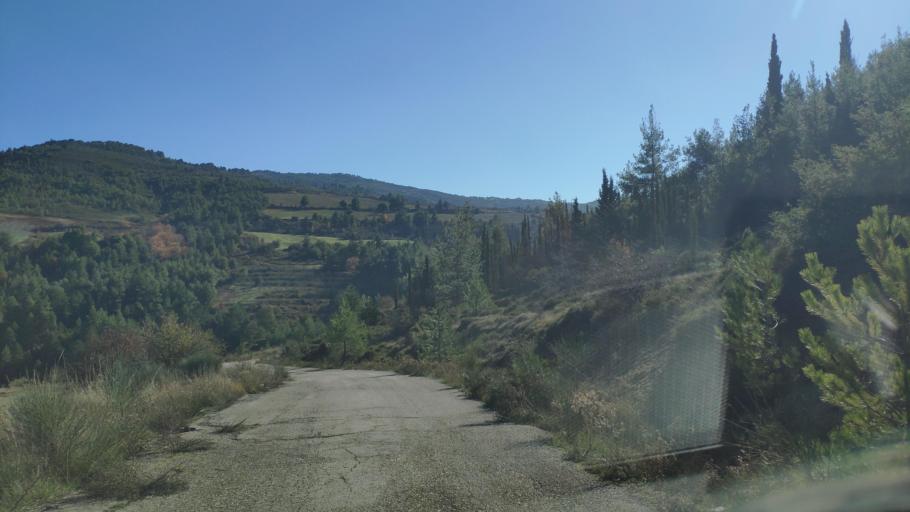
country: GR
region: West Greece
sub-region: Nomos Achaias
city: Aiyira
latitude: 38.0615
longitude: 22.4604
